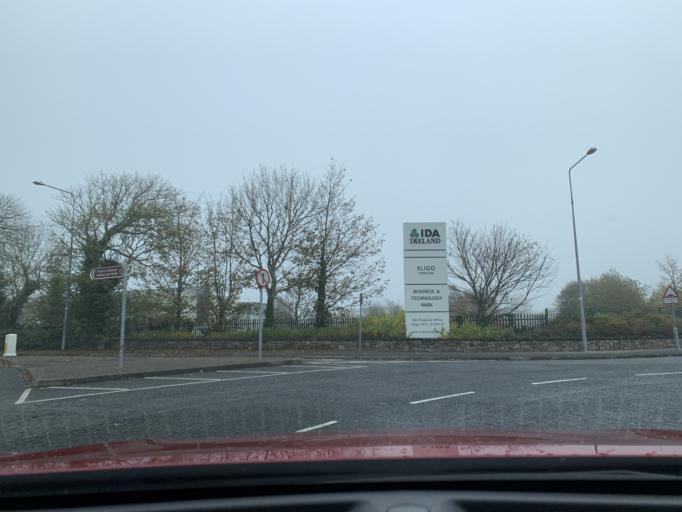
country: IE
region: Connaught
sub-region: Sligo
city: Sligo
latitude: 54.2772
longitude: -8.5025
